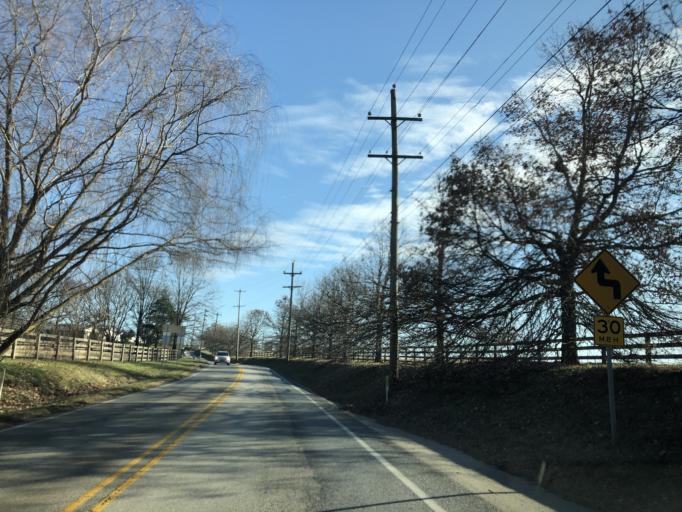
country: US
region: Pennsylvania
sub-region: Chester County
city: Toughkenamon
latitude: 39.8453
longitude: -75.7657
